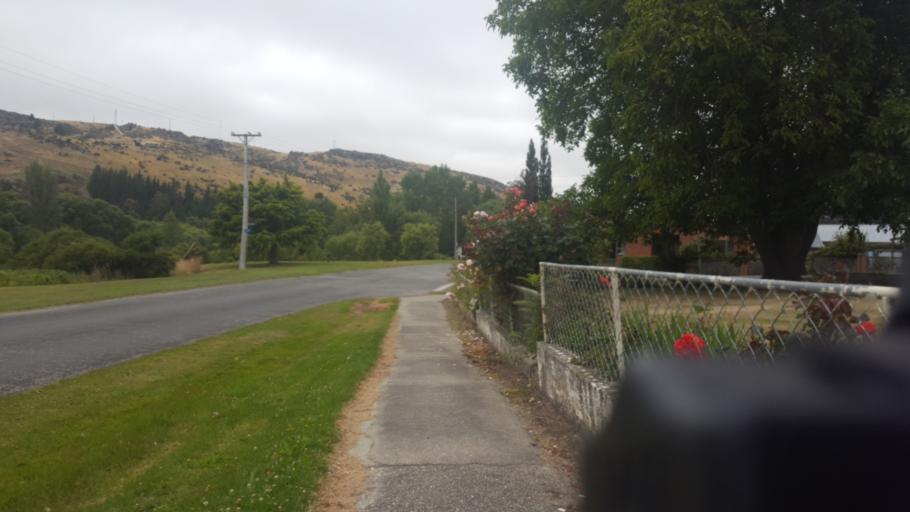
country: NZ
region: Otago
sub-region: Queenstown-Lakes District
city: Kingston
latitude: -45.5391
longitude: 169.3149
